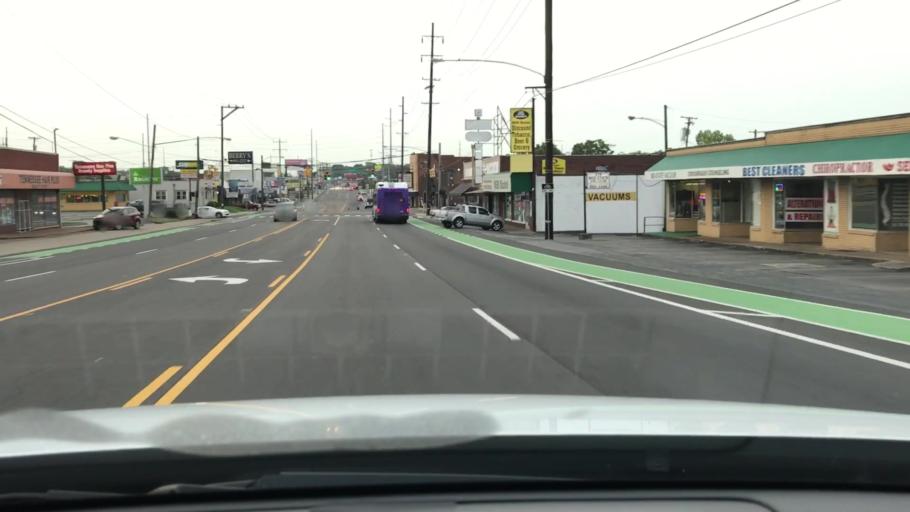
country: US
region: Tennessee
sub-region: Davidson County
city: Goodlettsville
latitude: 36.2575
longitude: -86.7138
